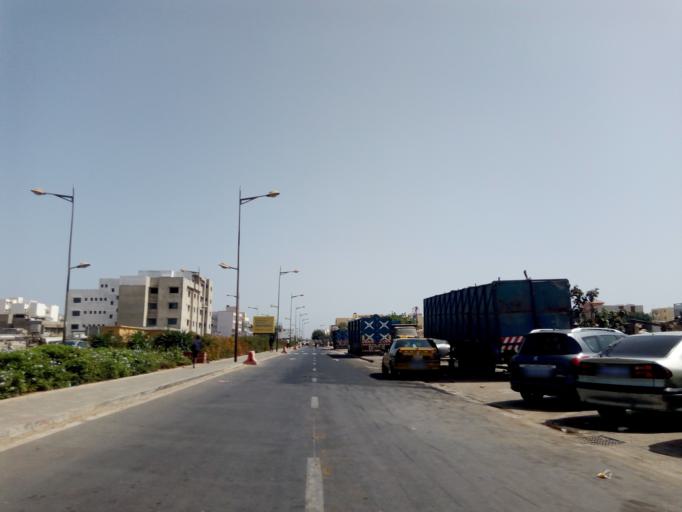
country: SN
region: Dakar
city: Dakar
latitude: 14.7022
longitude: -17.4510
